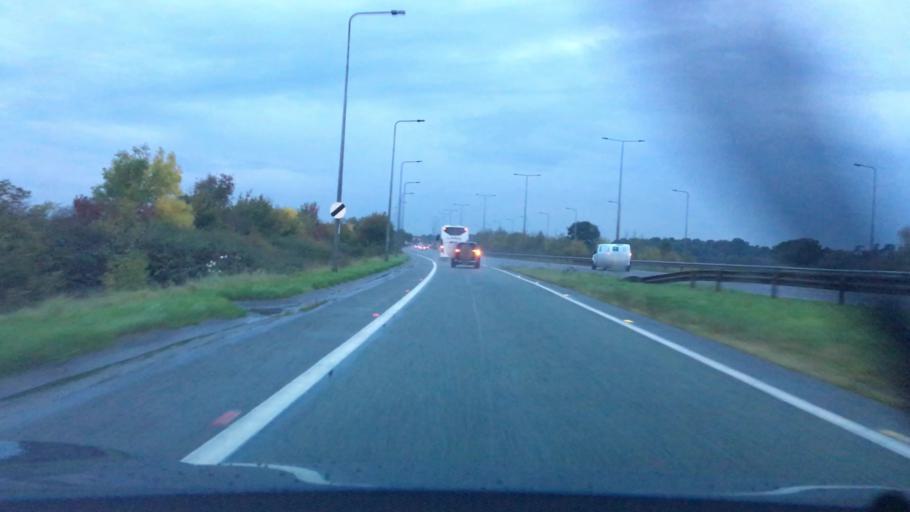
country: GB
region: England
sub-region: Derbyshire
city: Borrowash
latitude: 52.8738
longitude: -1.4000
